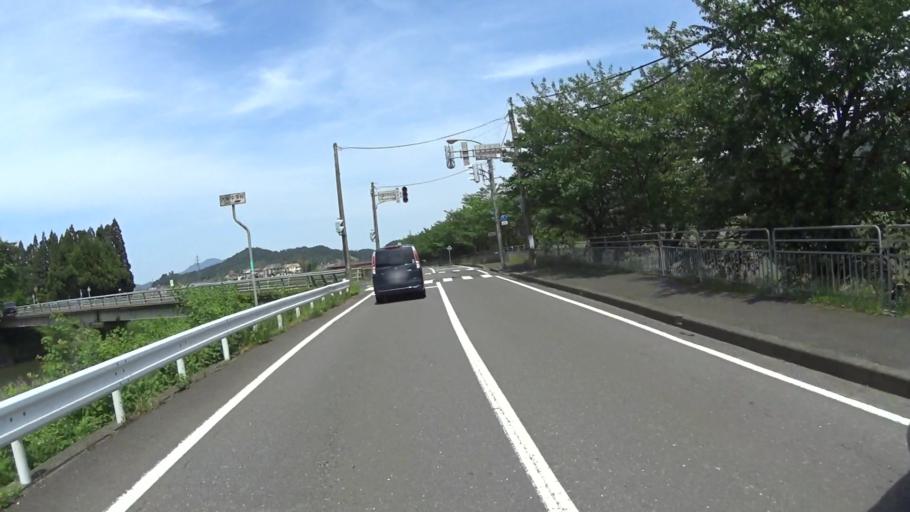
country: JP
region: Fukui
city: Obama
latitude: 35.4603
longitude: 135.6091
